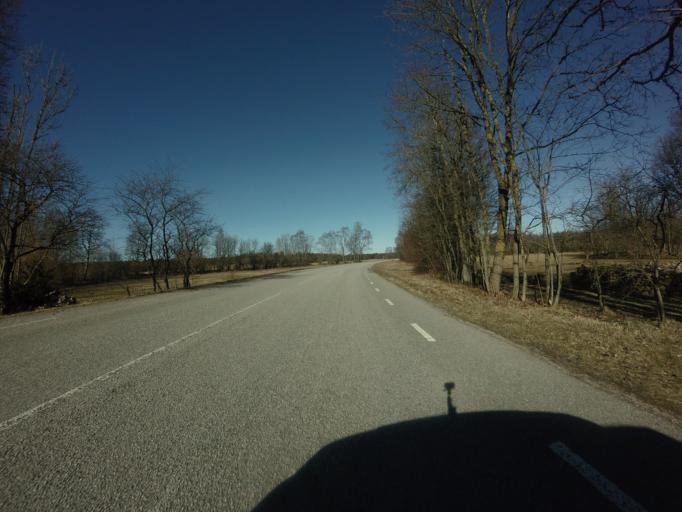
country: EE
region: Saare
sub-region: Kuressaare linn
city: Kuressaare
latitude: 58.4736
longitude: 22.2278
